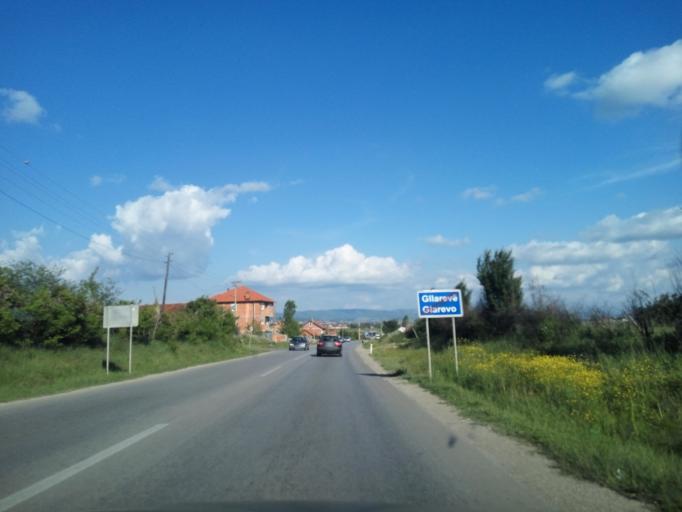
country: XK
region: Prizren
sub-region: Komuna e Malisheves
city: Llazice
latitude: 42.5861
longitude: 20.6866
